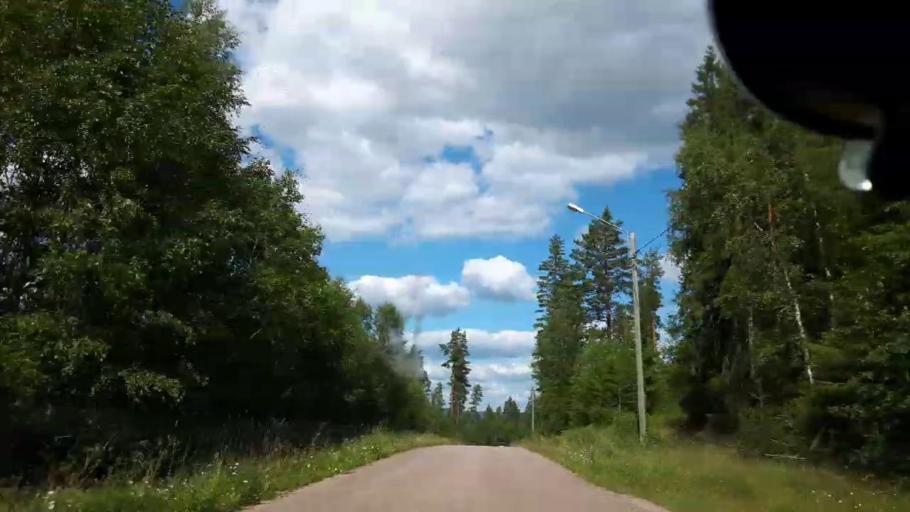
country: SE
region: Jaemtland
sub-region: Ragunda Kommun
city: Hammarstrand
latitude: 62.9319
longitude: 16.6936
